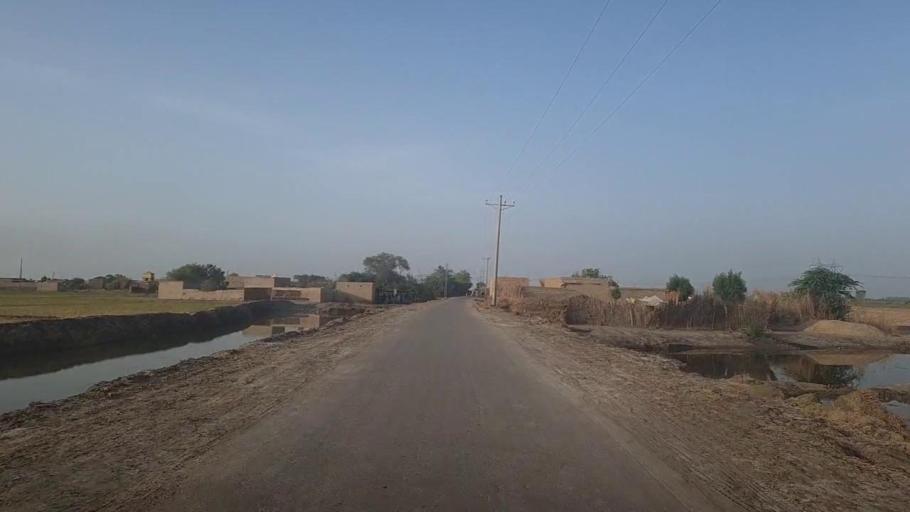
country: PK
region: Sindh
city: Radhan
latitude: 27.1163
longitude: 67.9141
